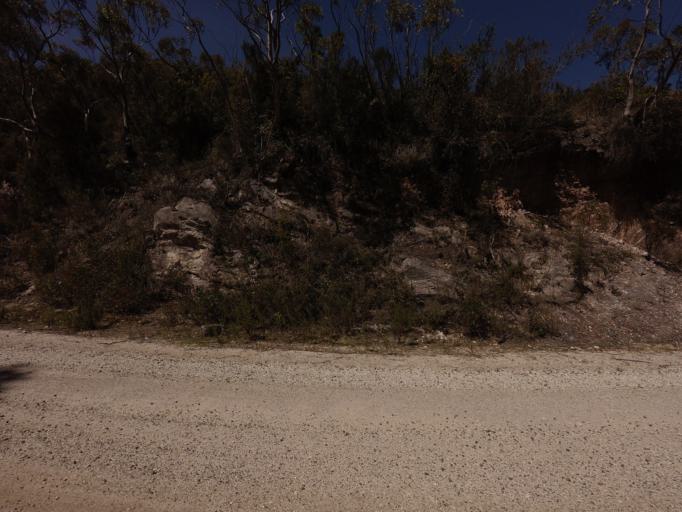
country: AU
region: Tasmania
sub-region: Huon Valley
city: Geeveston
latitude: -42.9257
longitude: 146.3473
